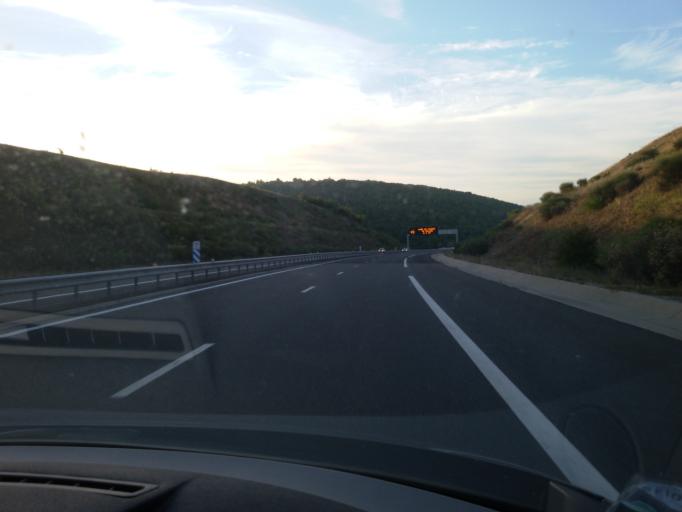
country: FR
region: Midi-Pyrenees
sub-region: Departement de l'Aveyron
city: Creissels
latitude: 44.0606
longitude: 3.0292
